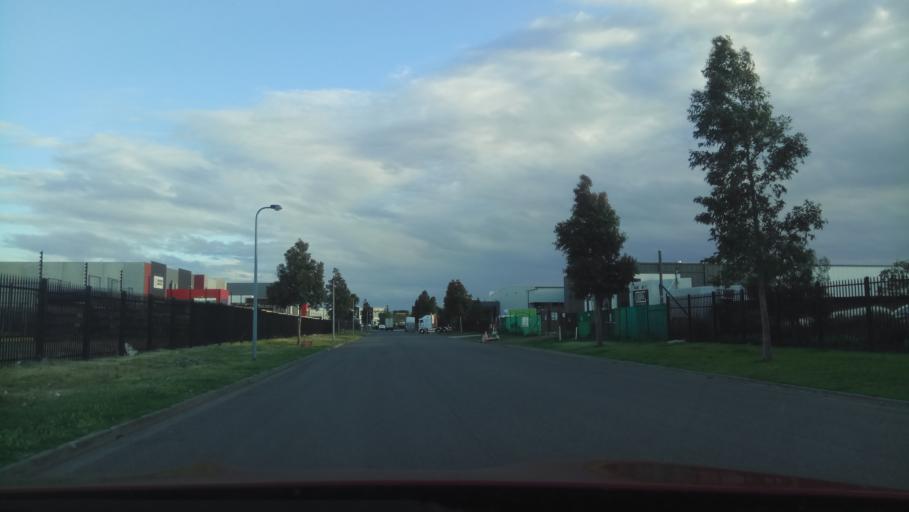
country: AU
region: Victoria
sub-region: Hobsons Bay
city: Altona
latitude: -37.8527
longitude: 144.8254
